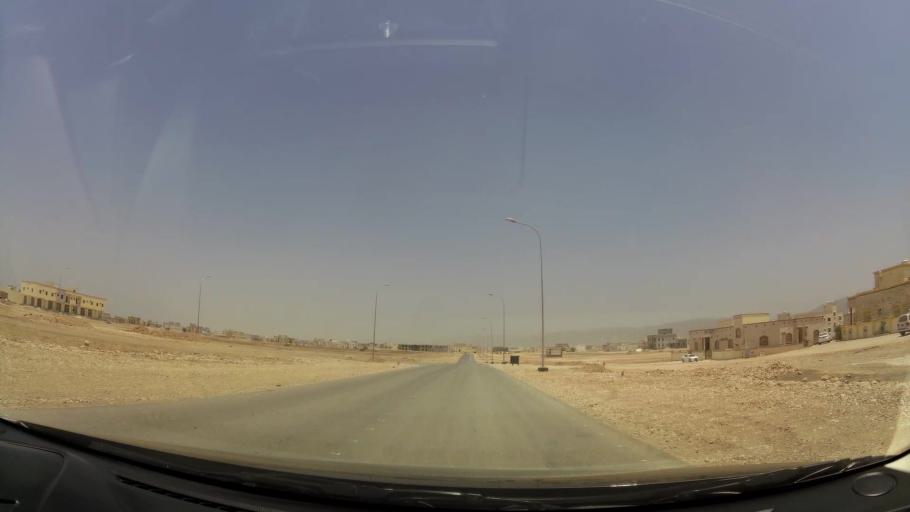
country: OM
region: Zufar
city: Salalah
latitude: 17.0976
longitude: 54.1773
